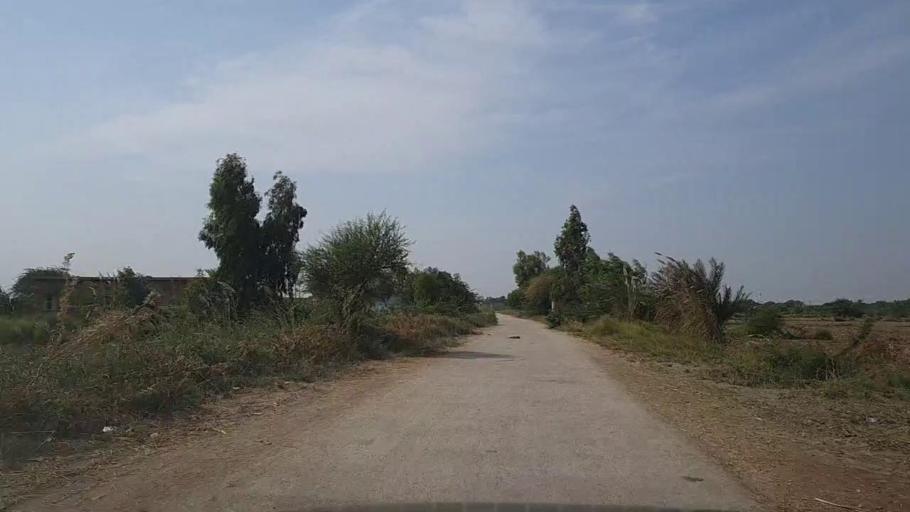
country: PK
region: Sindh
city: Thatta
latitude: 24.7835
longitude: 67.8356
